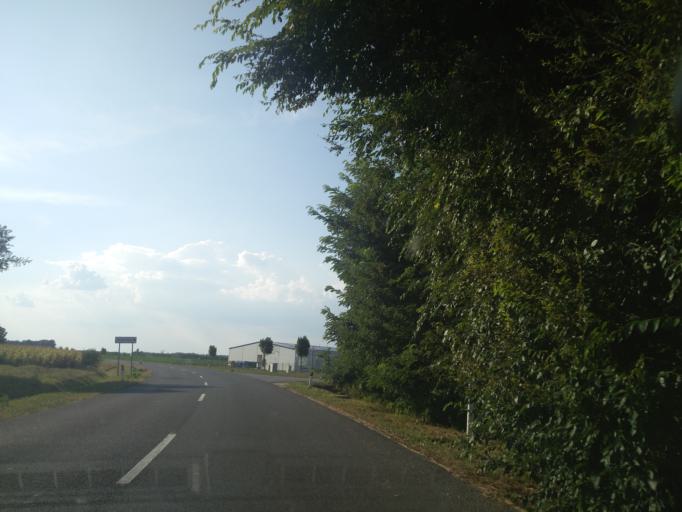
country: HU
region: Zala
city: Zalaegerszeg
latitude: 46.8797
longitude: 16.8294
